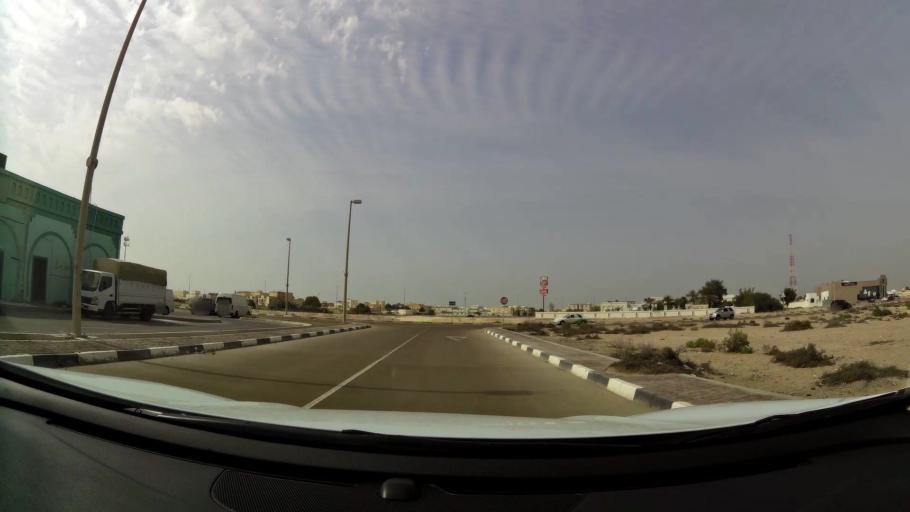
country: AE
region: Abu Dhabi
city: Abu Dhabi
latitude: 24.5457
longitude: 54.6869
